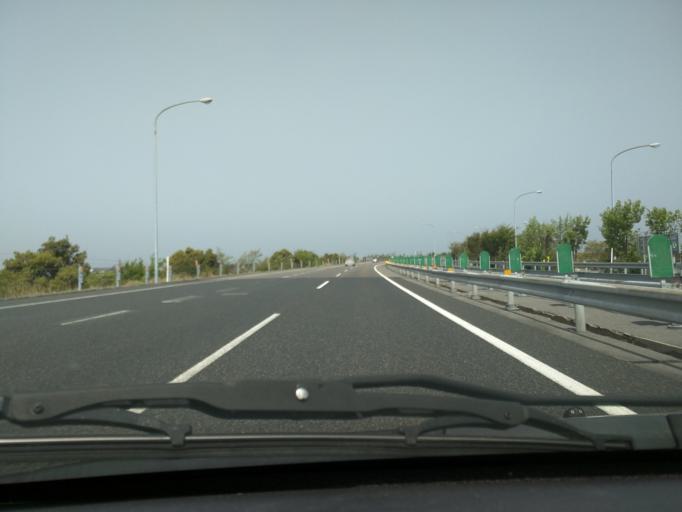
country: JP
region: Niigata
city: Kameda-honcho
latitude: 37.8490
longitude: 139.0593
